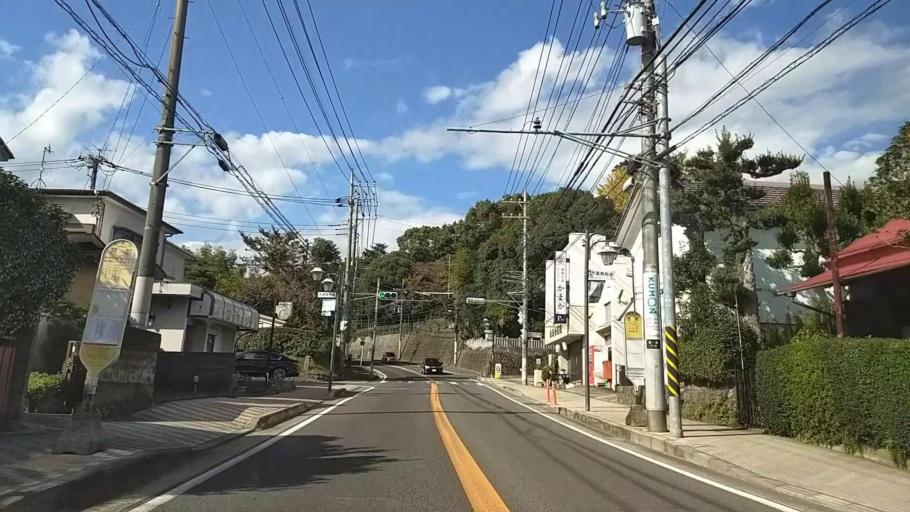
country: JP
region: Kanagawa
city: Hadano
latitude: 35.3790
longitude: 139.2209
